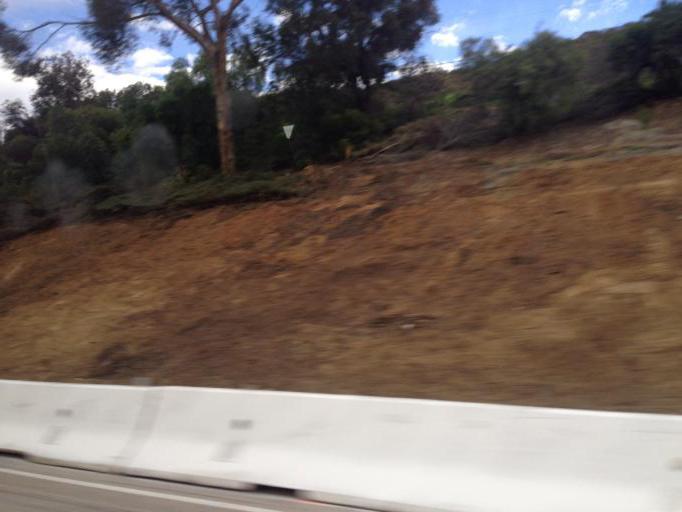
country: US
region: California
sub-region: San Diego County
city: National City
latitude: 32.6701
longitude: -117.0813
